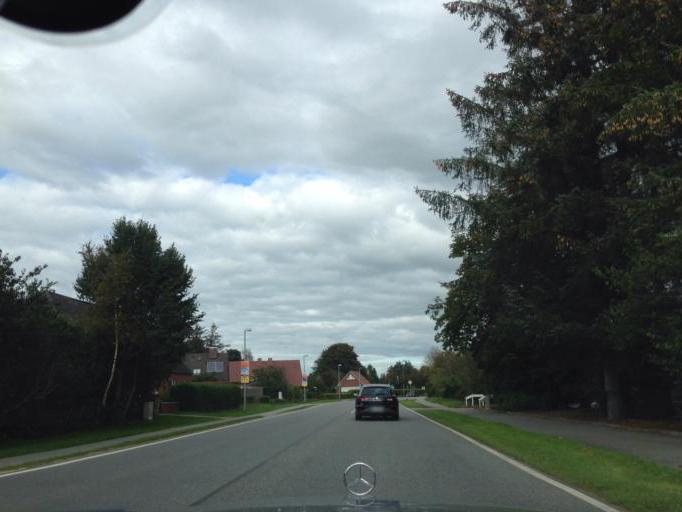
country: DE
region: Schleswig-Holstein
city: Leck
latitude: 54.7630
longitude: 8.9780
